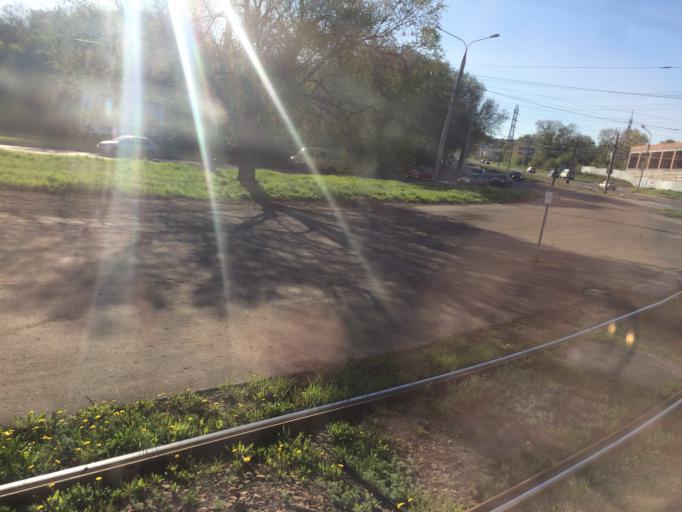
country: RU
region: Chelyabinsk
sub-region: Gorod Magnitogorsk
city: Magnitogorsk
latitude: 53.4000
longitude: 59.0409
